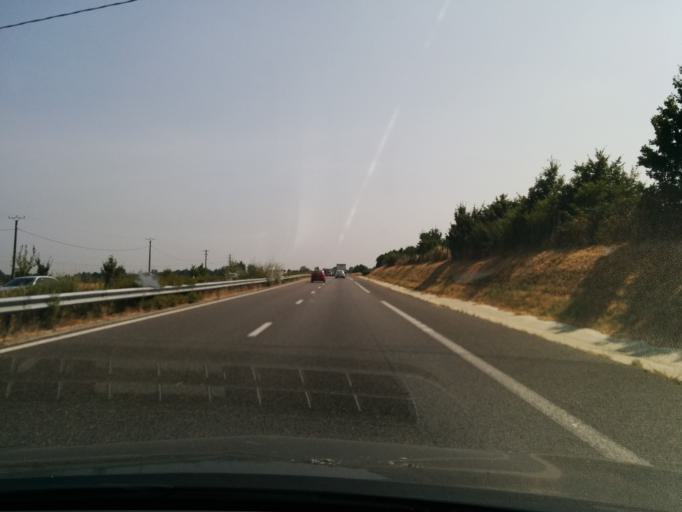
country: FR
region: Midi-Pyrenees
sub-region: Departement du Tarn
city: Giroussens
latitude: 43.8015
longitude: 1.7721
